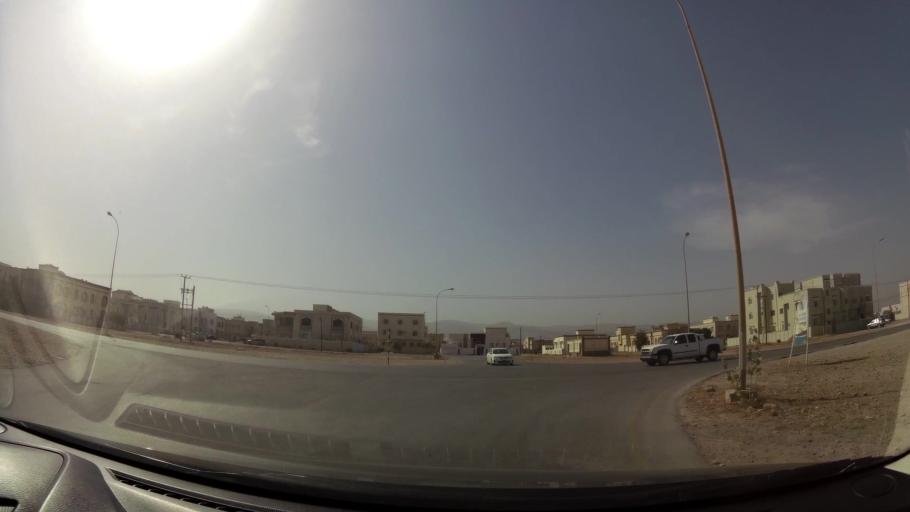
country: OM
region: Zufar
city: Salalah
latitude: 17.0034
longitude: 54.0125
